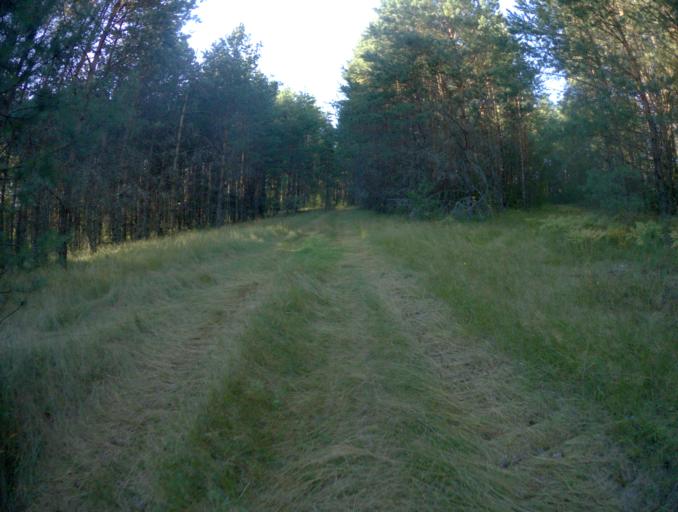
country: RU
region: Vladimir
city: Krasnaya Gorbatka
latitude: 55.7905
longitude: 41.6533
